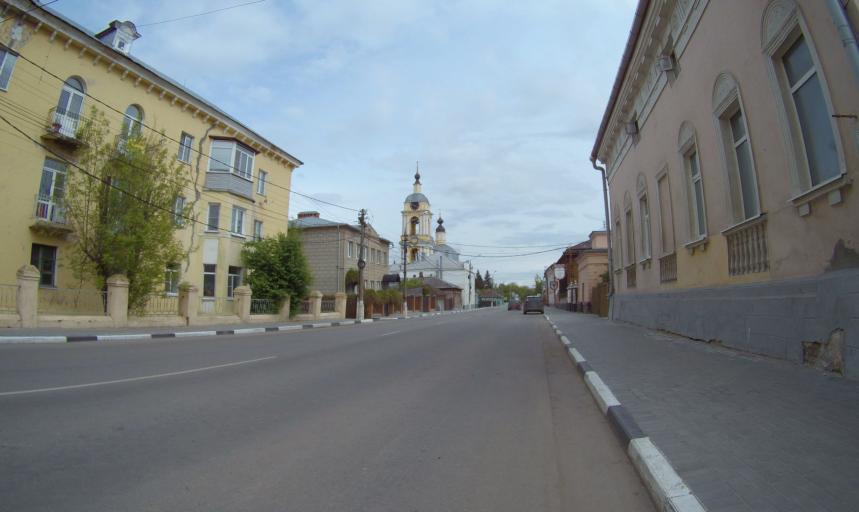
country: RU
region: Moskovskaya
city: Kolomna
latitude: 55.1012
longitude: 38.7605
